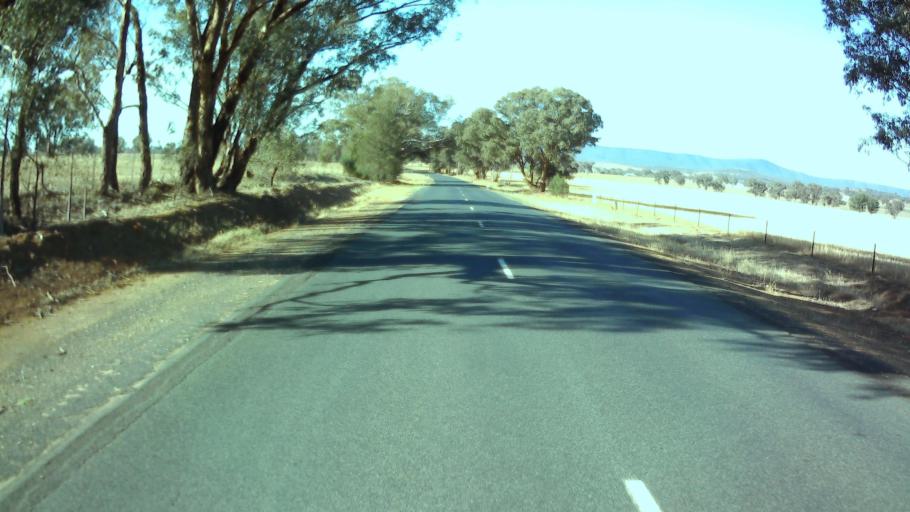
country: AU
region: New South Wales
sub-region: Weddin
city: Grenfell
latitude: -33.9219
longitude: 148.1399
